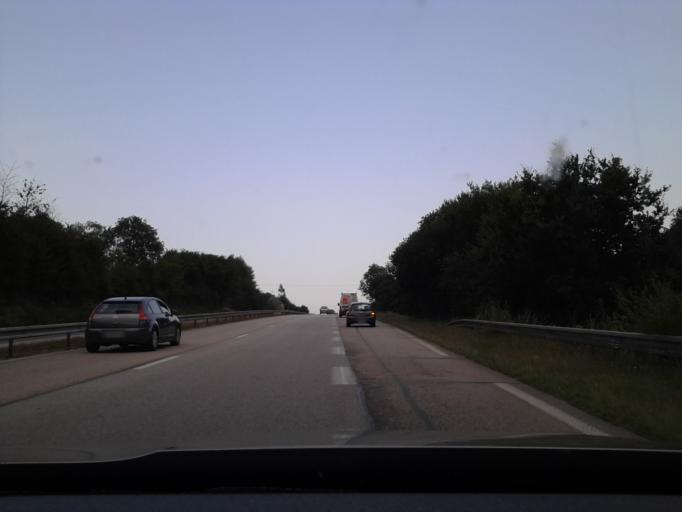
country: FR
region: Lower Normandy
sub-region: Departement de la Manche
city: Valognes
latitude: 49.5233
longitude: -1.5050
